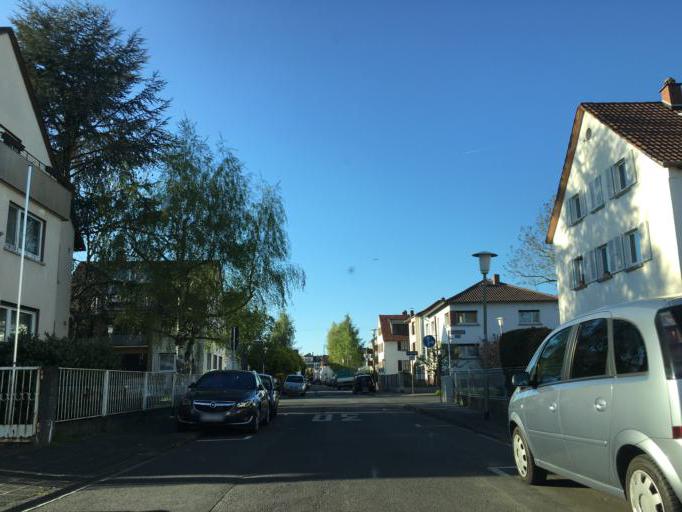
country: DE
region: Hesse
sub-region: Regierungsbezirk Darmstadt
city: Offenbach
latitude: 50.0981
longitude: 8.7700
